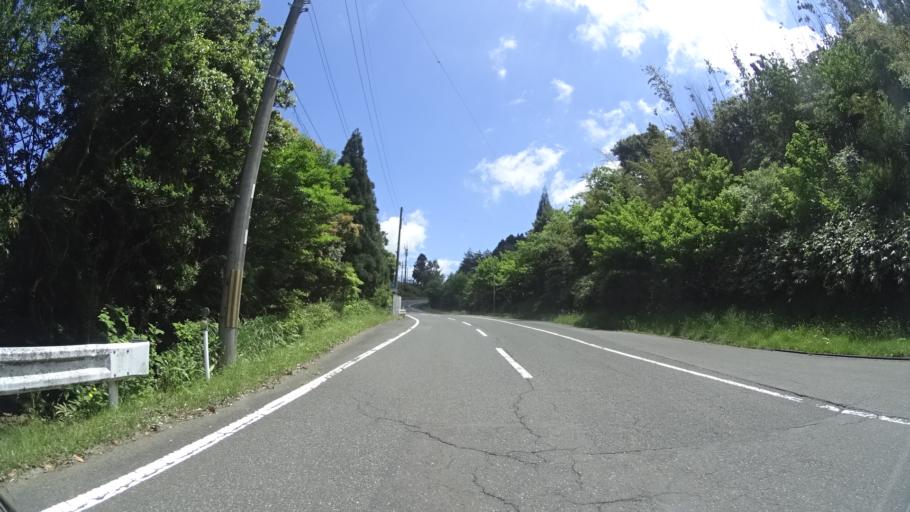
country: JP
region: Kyoto
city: Miyazu
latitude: 35.4782
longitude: 135.1614
